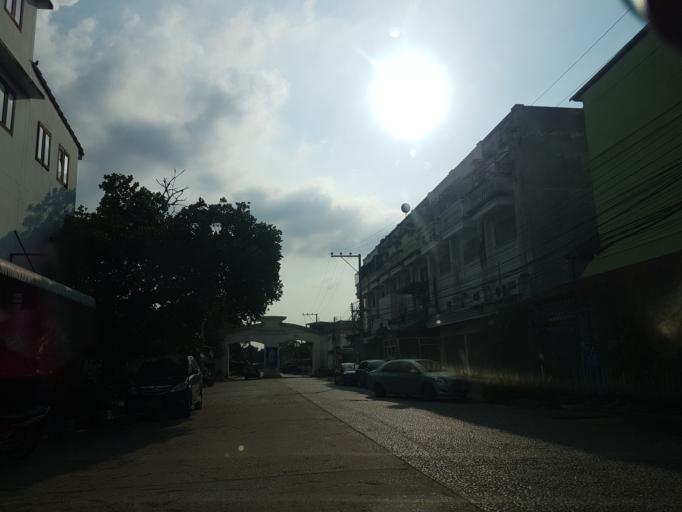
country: TH
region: Lop Buri
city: Lop Buri
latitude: 14.7734
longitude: 100.6985
